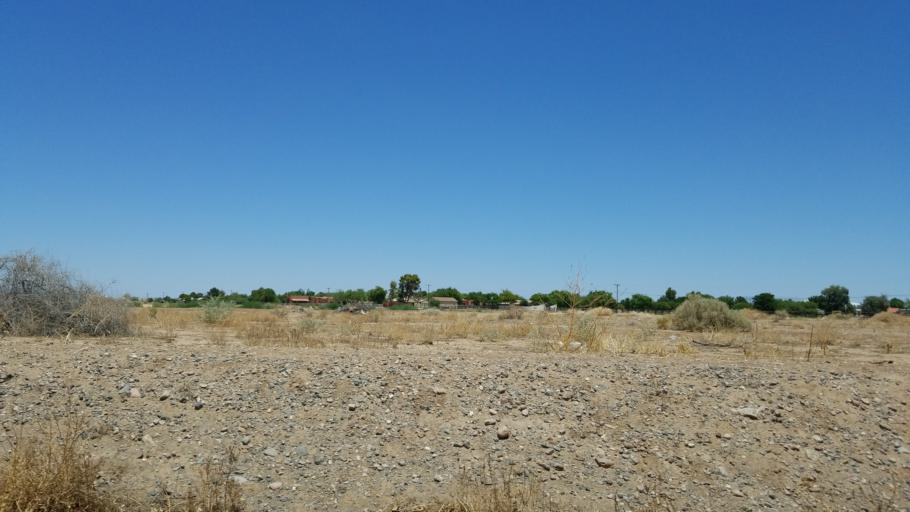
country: US
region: Arizona
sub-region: Maricopa County
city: Litchfield Park
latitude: 33.5148
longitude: -112.2915
